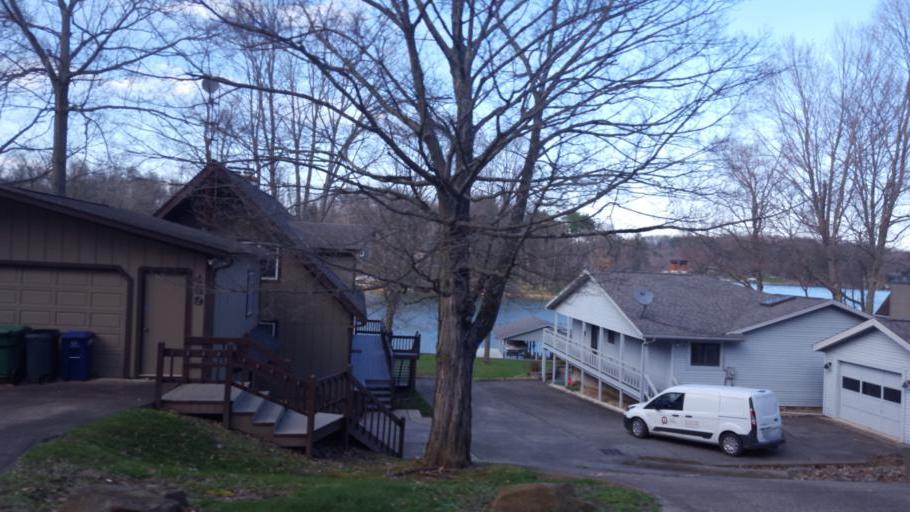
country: US
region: Ohio
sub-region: Knox County
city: Gambier
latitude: 40.4305
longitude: -82.3533
